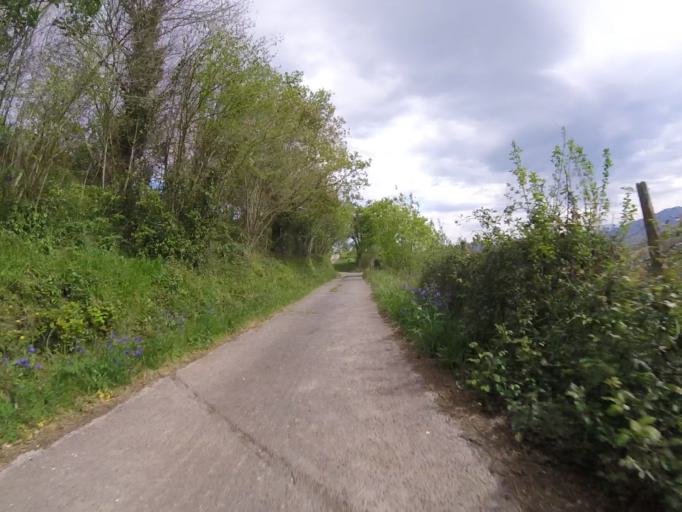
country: ES
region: Basque Country
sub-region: Provincia de Guipuzcoa
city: Zarautz
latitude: 43.2539
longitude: -2.1785
